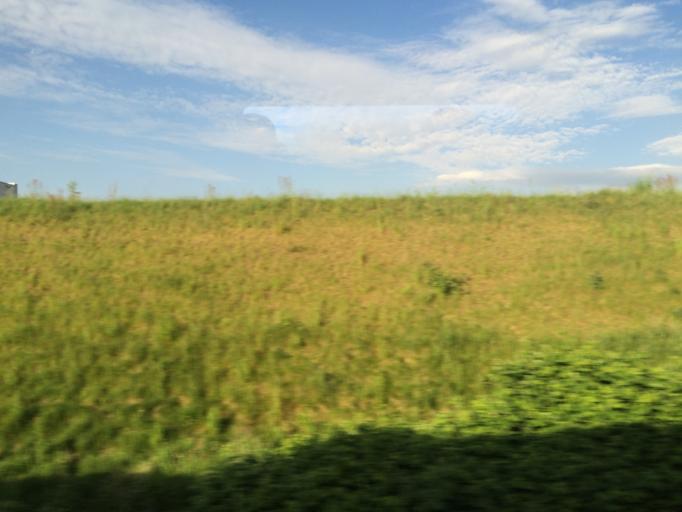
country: DE
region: North Rhine-Westphalia
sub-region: Regierungsbezirk Dusseldorf
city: Langenfeld
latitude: 51.1224
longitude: 6.9192
